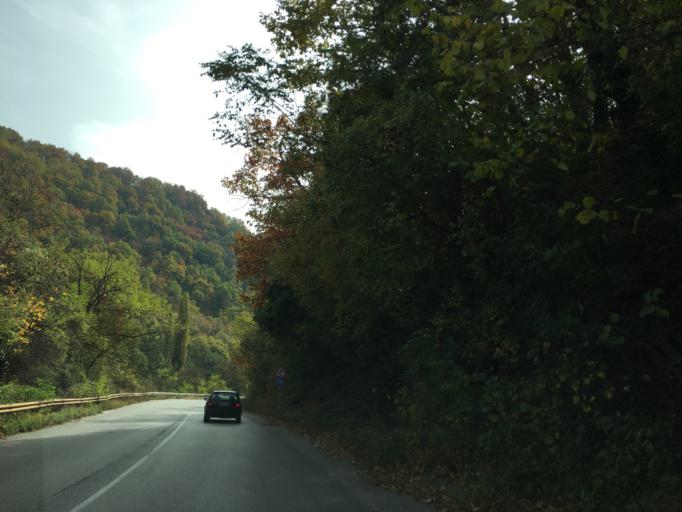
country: BG
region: Sofia-Capital
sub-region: Stolichna Obshtina
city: Sofia
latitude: 42.5648
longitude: 23.4244
